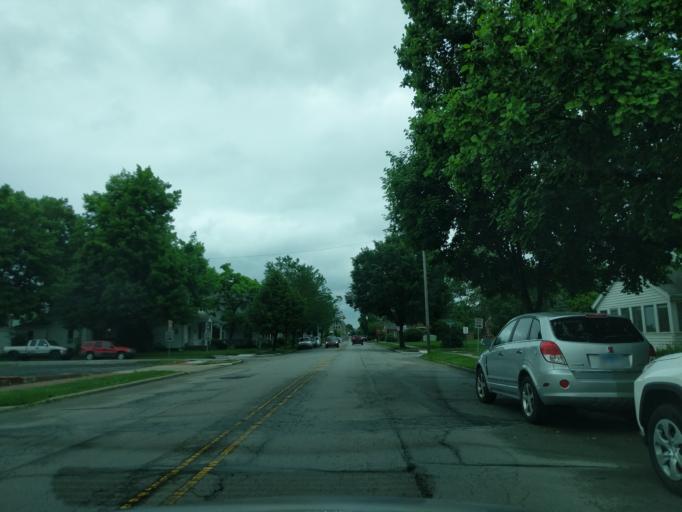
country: US
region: Indiana
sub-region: Hamilton County
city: Noblesville
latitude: 40.0419
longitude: -86.0122
